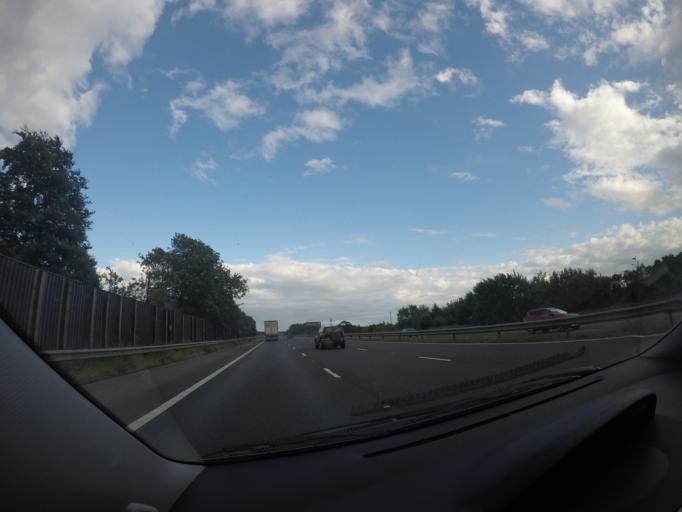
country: GB
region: England
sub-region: Cumbria
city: Carlisle
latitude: 54.9576
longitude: -2.9876
